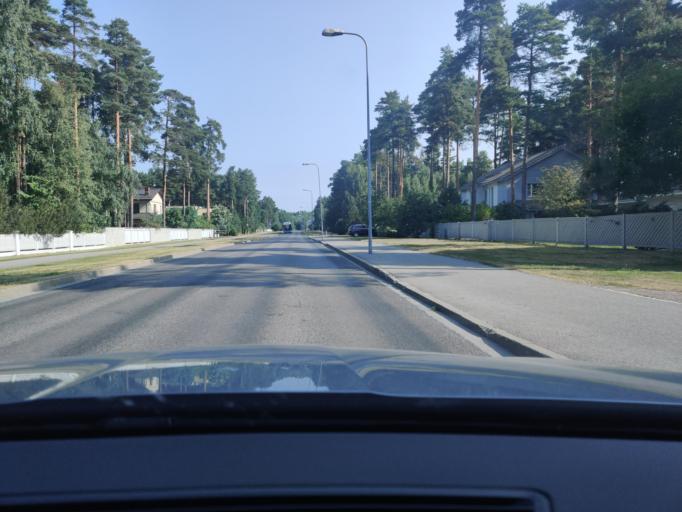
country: EE
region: Harju
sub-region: Saue vald
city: Laagri
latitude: 59.3571
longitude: 24.6114
